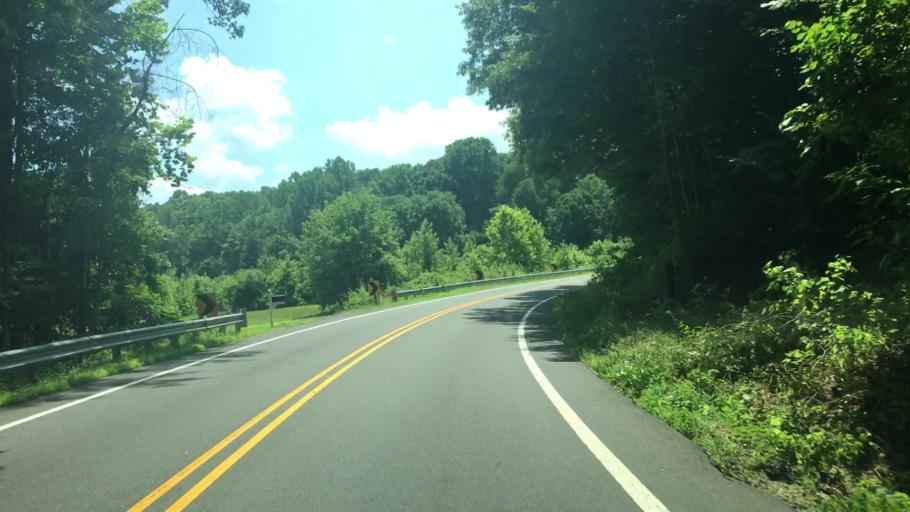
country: US
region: Virginia
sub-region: King George County
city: Passapatanzy
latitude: 38.2994
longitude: -77.2983
